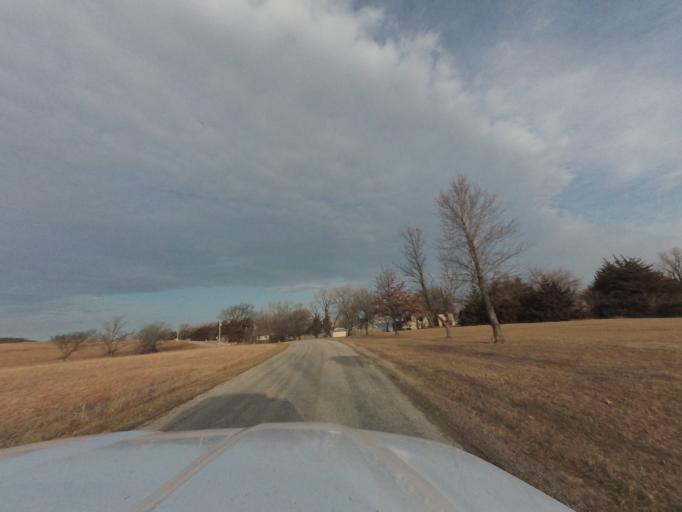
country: US
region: Kansas
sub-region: Morris County
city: Council Grove
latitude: 38.5184
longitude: -96.4167
